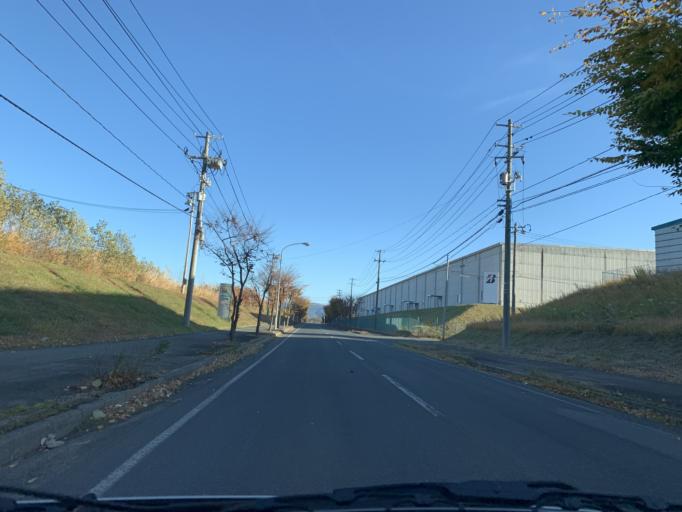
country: JP
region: Iwate
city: Mizusawa
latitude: 39.2077
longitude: 141.1802
